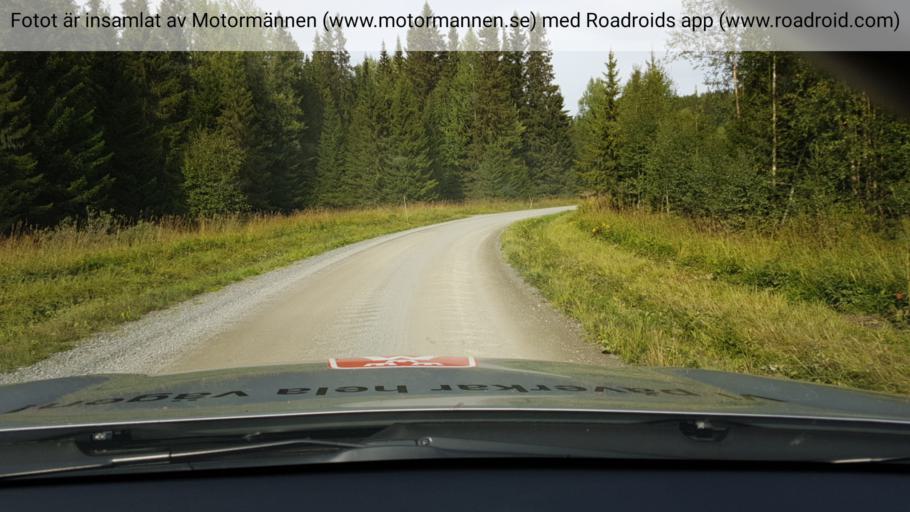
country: SE
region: Jaemtland
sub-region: Krokoms Kommun
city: Valla
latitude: 63.3864
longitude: 14.0436
